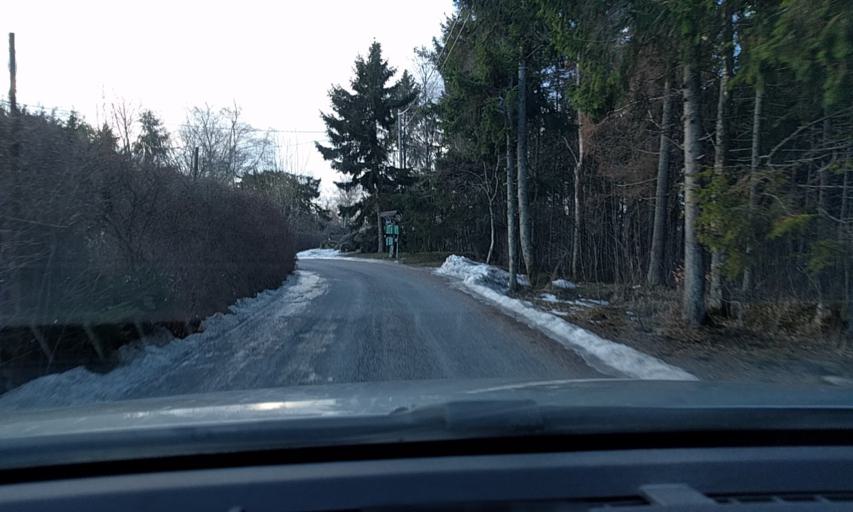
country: EE
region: Harju
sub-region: Viimsi vald
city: Viimsi
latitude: 59.5140
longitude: 24.9059
